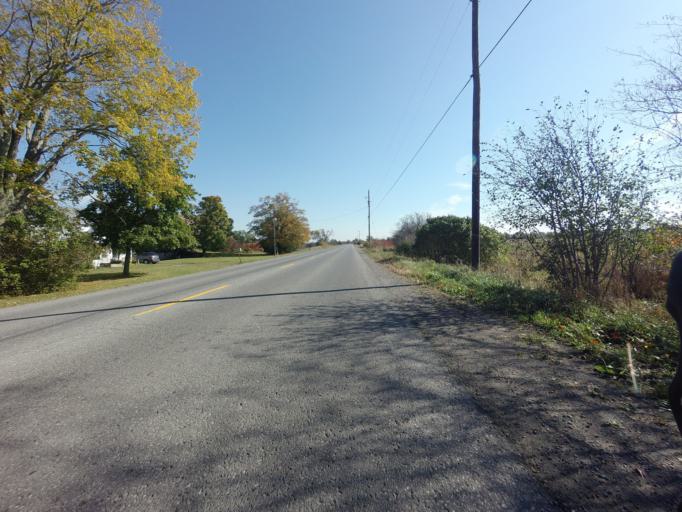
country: CA
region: Ontario
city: Prince Edward
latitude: 44.0108
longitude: -77.3574
